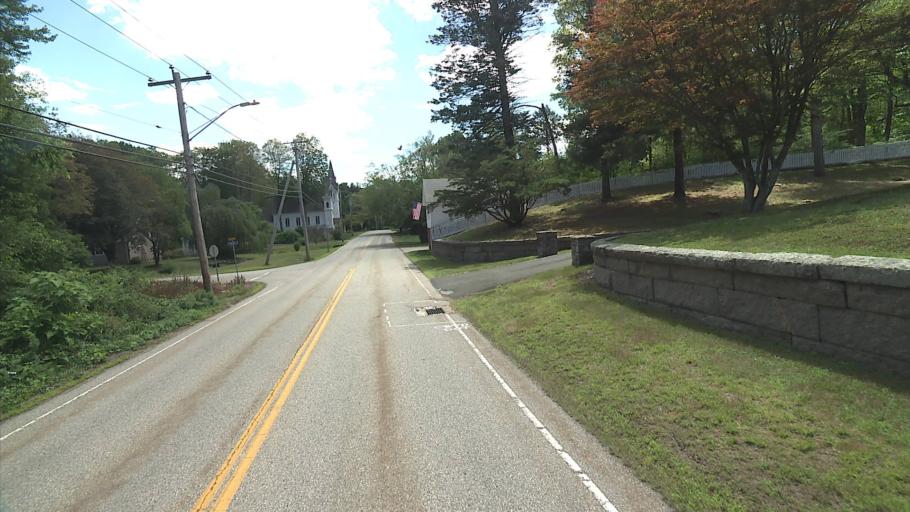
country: US
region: Connecticut
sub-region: Middlesex County
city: East Hampton
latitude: 41.5570
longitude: -72.5529
